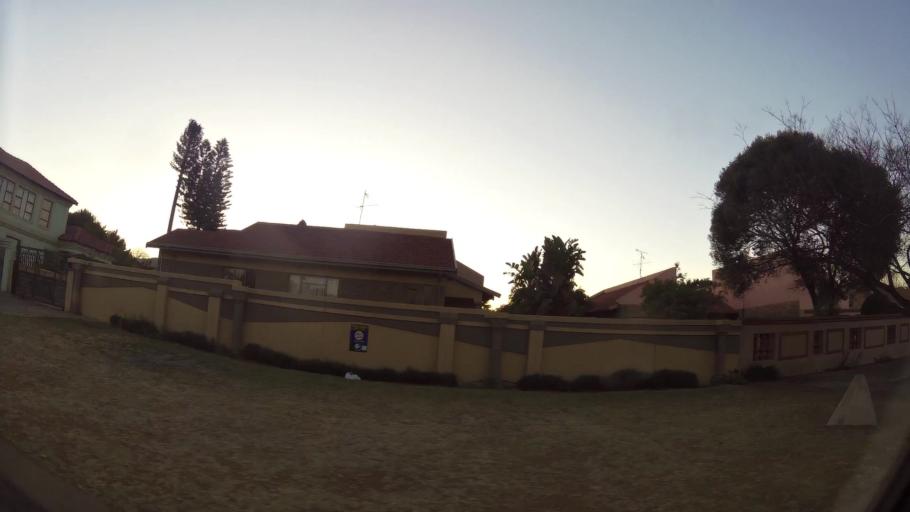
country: ZA
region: North-West
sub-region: Bojanala Platinum District Municipality
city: Rustenburg
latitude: -25.6632
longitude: 27.2174
